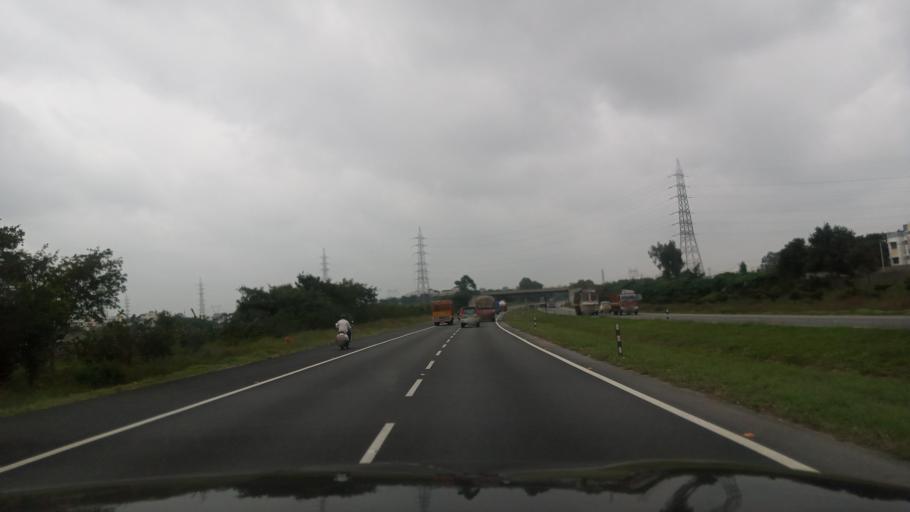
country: IN
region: Karnataka
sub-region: Bangalore Urban
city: Bangalore
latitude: 12.8670
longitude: 77.6356
